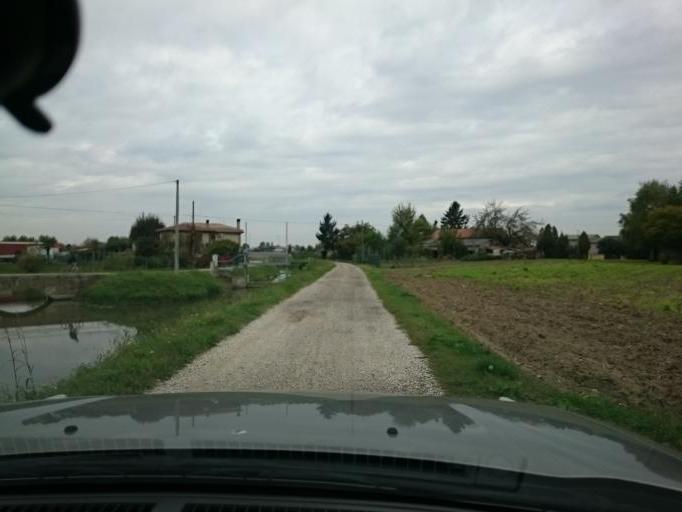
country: IT
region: Veneto
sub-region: Provincia di Padova
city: Codevigo
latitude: 45.2661
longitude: 12.0905
